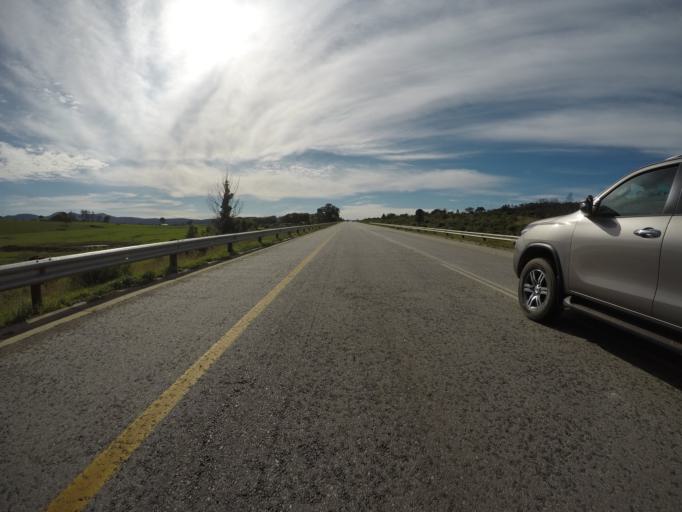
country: ZA
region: Eastern Cape
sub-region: Cacadu District Municipality
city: Jeffrey's Bay
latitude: -33.9010
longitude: 25.1139
